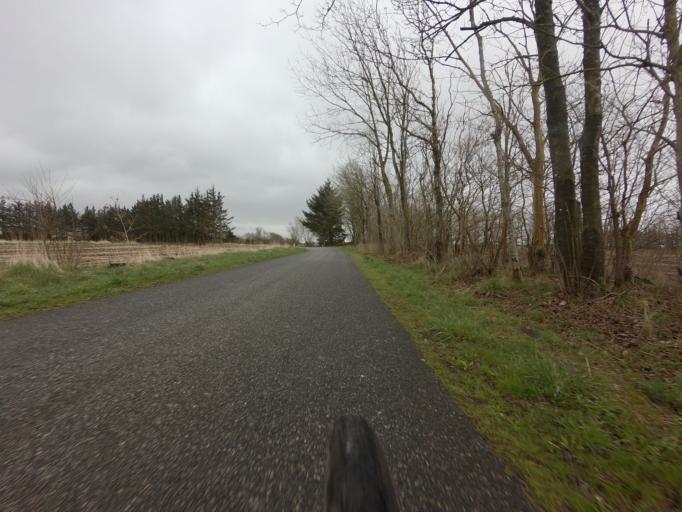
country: DK
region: North Denmark
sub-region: Jammerbugt Kommune
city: Pandrup
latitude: 57.3260
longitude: 9.7859
